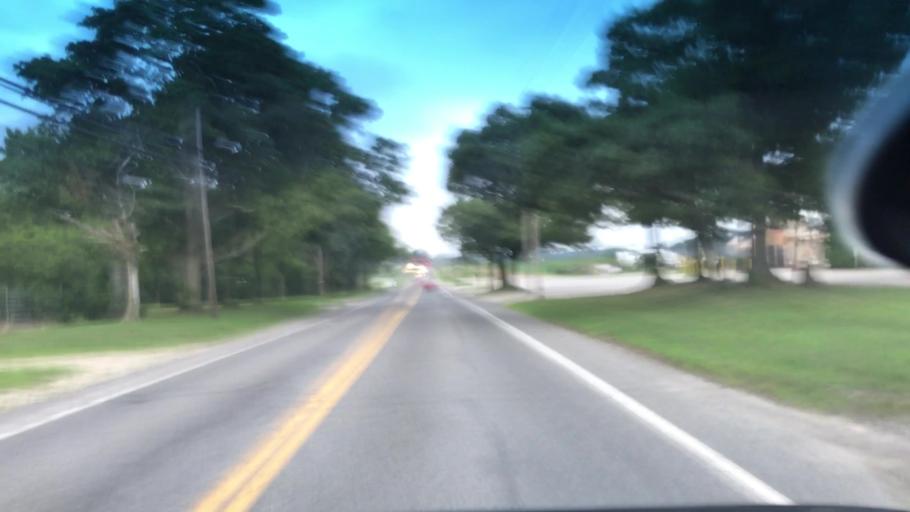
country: US
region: New York
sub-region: Suffolk County
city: Wading River
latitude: 40.9473
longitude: -72.8113
